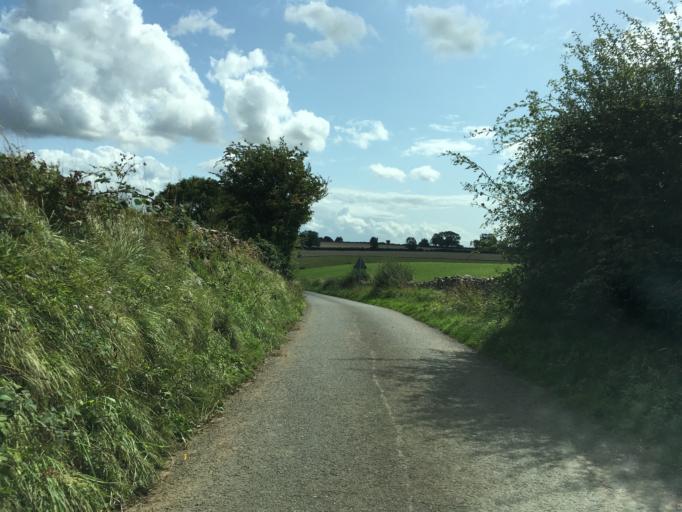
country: GB
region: England
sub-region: Wiltshire
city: Luckington
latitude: 51.6109
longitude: -2.2530
